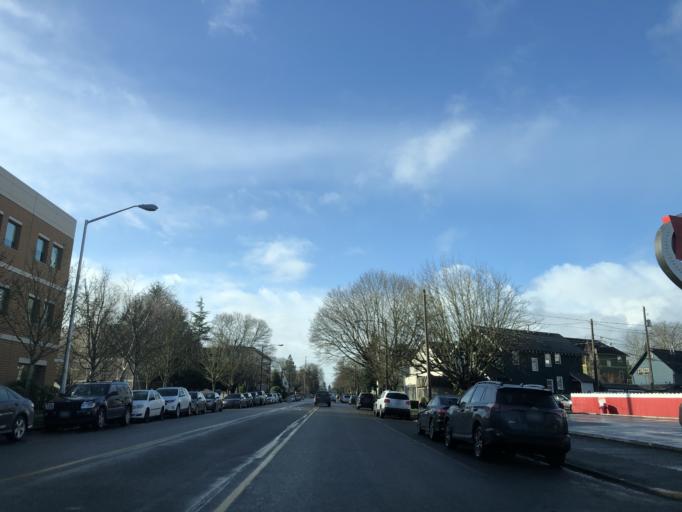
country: US
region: Washington
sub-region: Pierce County
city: Tacoma
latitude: 47.2601
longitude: -122.4551
